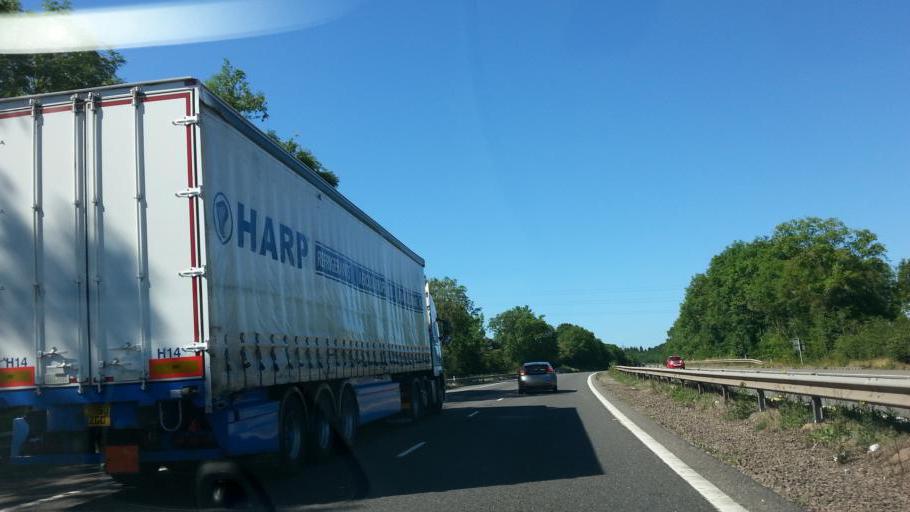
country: GB
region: England
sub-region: Gloucestershire
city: Newent
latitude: 51.9611
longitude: -2.4321
